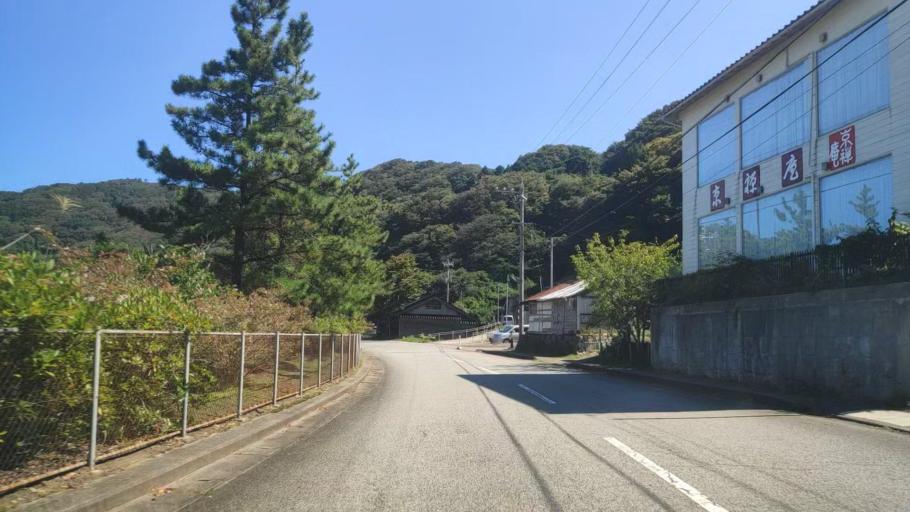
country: JP
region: Ishikawa
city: Nanao
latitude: 37.5190
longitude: 137.2413
